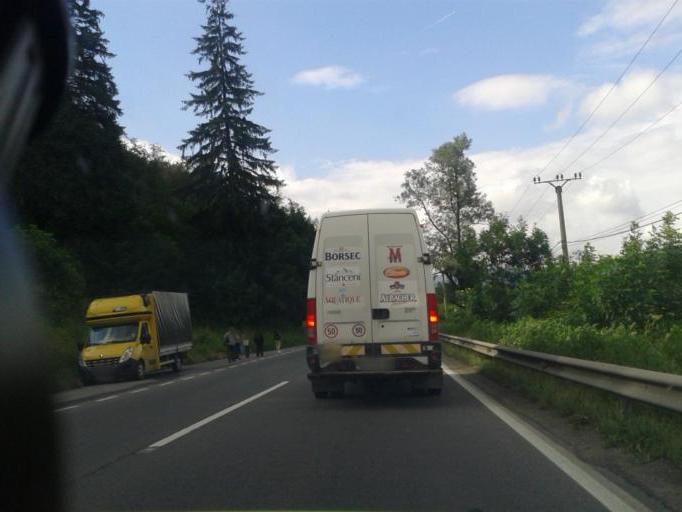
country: RO
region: Prahova
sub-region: Oras Busteni
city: Poiana Tapului
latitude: 45.3750
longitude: 25.5402
